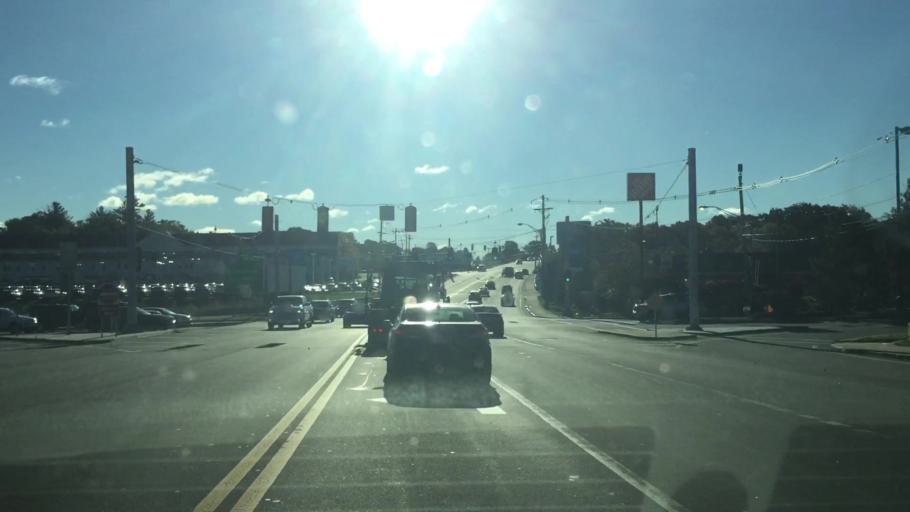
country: US
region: Massachusetts
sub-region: Middlesex County
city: Tewksbury
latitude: 42.6273
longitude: -71.2709
